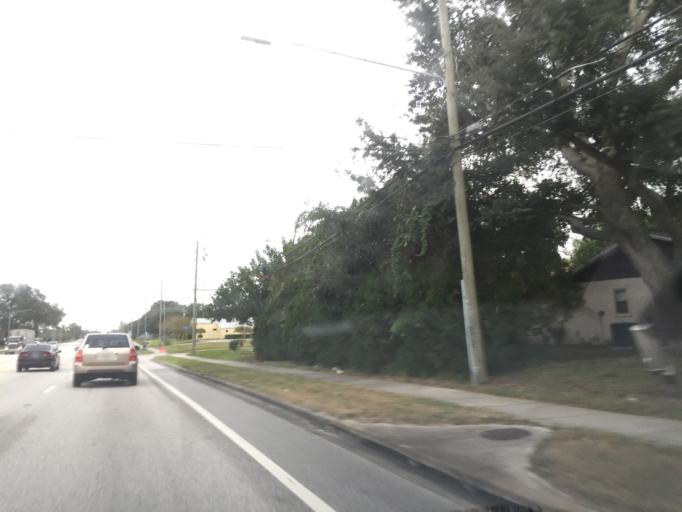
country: US
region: Florida
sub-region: Pinellas County
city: Safety Harbor
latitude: 27.9679
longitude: -82.7392
